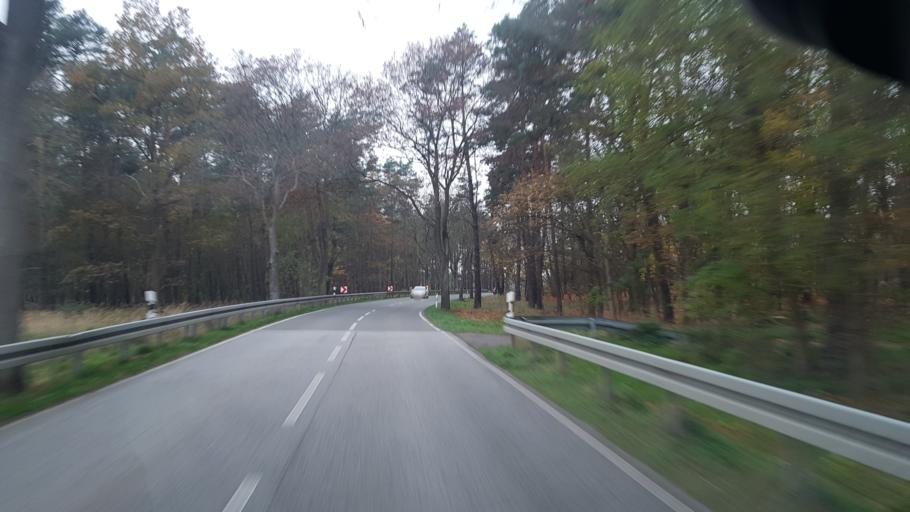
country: DE
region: Brandenburg
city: Ruthnick
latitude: 52.8999
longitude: 12.9606
